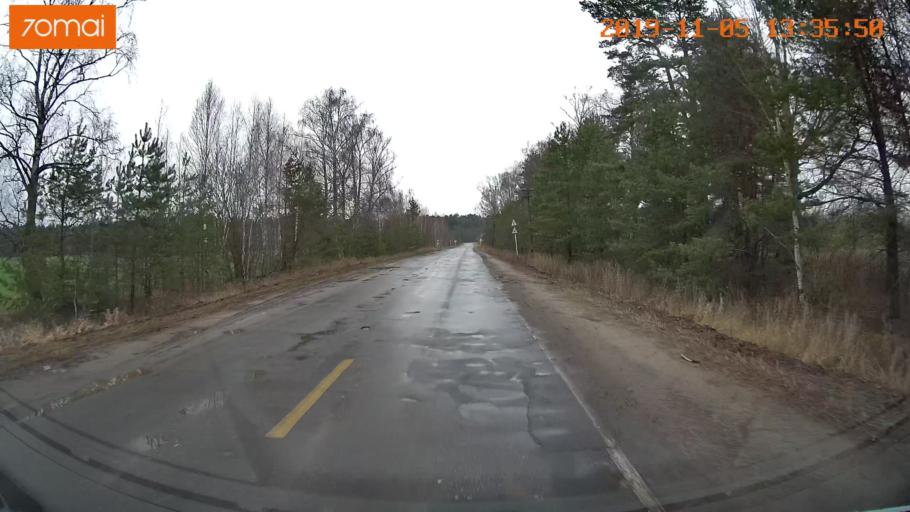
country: RU
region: Ivanovo
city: Shuya
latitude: 56.9106
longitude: 41.3852
